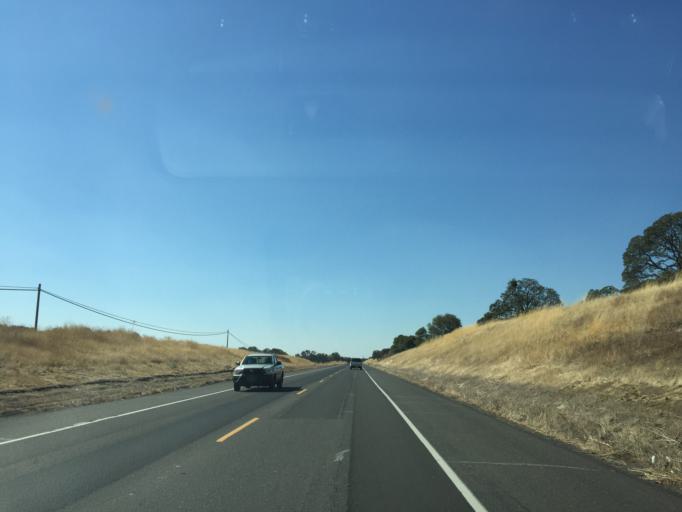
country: US
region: California
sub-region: Tuolumne County
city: Jamestown
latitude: 37.9120
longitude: -120.4632
